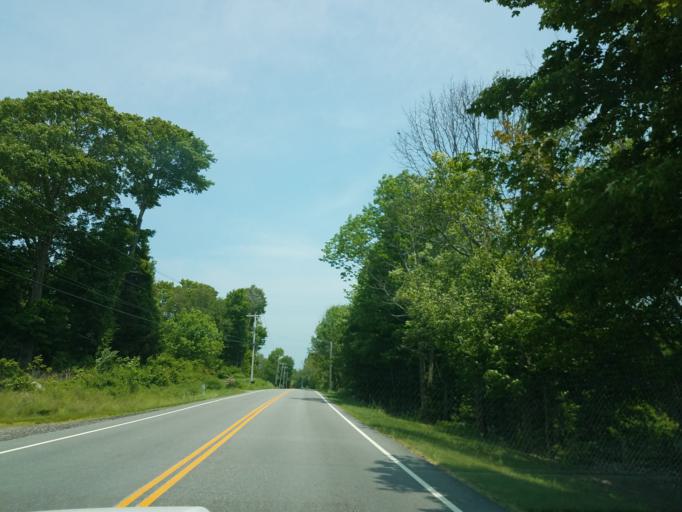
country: US
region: Connecticut
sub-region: Windham County
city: Moosup
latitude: 41.6592
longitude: -71.8474
